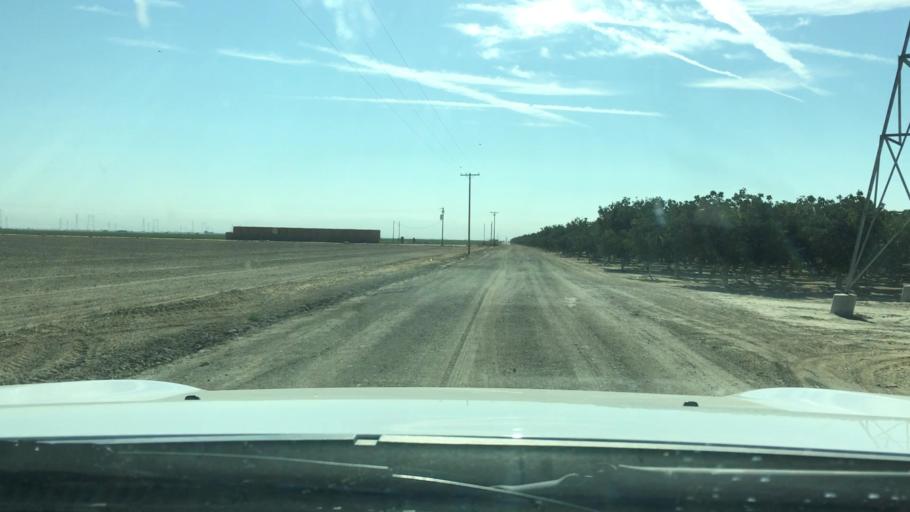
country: US
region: California
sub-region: Kern County
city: Buttonwillow
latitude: 35.3767
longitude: -119.3976
